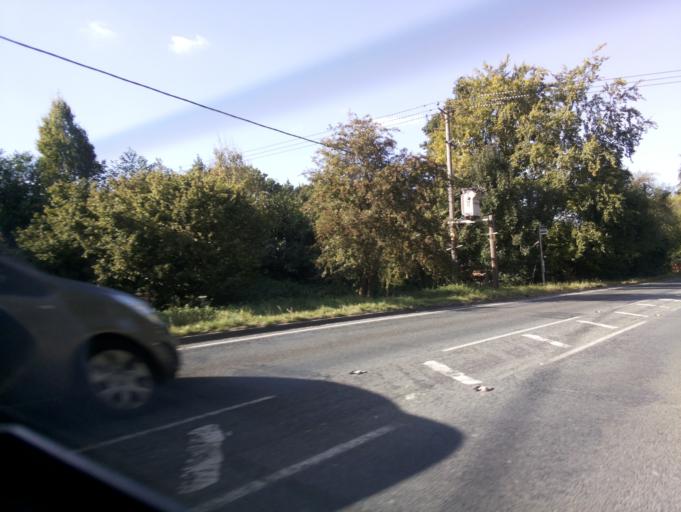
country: GB
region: England
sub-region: Hampshire
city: Tadley
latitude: 51.3284
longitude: -1.1287
